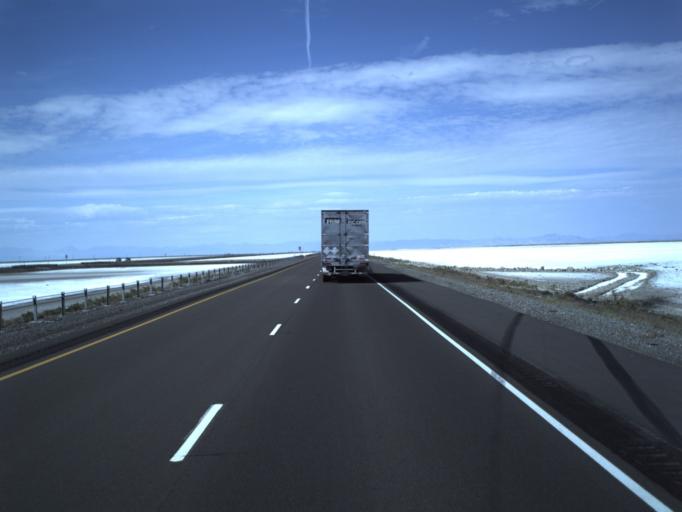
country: US
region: Utah
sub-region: Tooele County
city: Wendover
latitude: 40.7295
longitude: -113.4004
